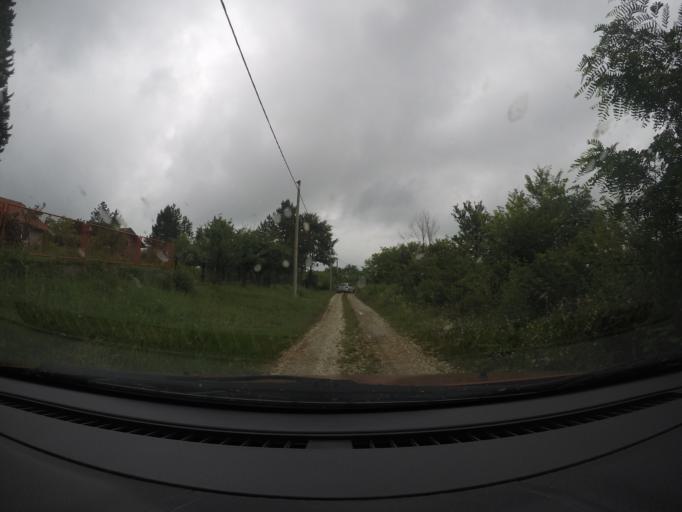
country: RS
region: Central Serbia
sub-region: Belgrade
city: Sopot
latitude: 44.5521
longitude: 20.5110
